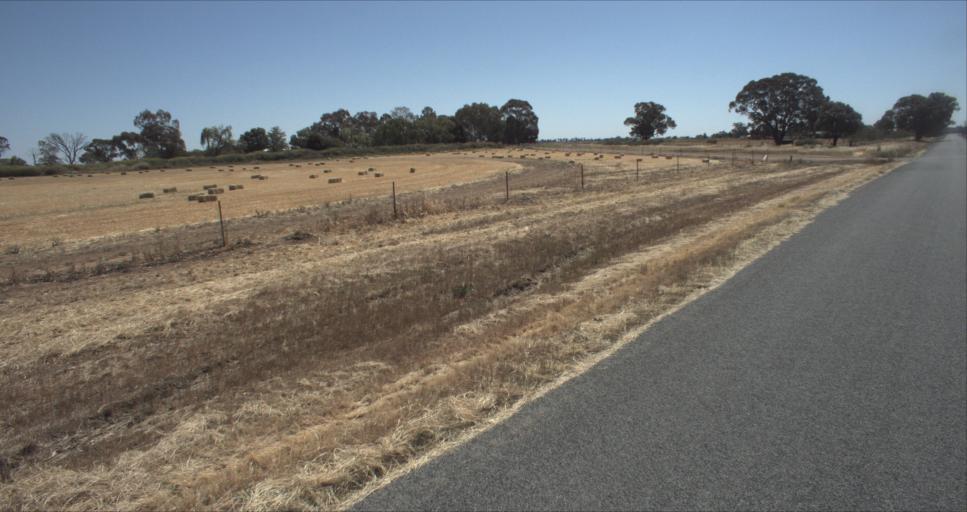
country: AU
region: New South Wales
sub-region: Leeton
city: Leeton
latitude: -34.5315
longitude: 146.4460
